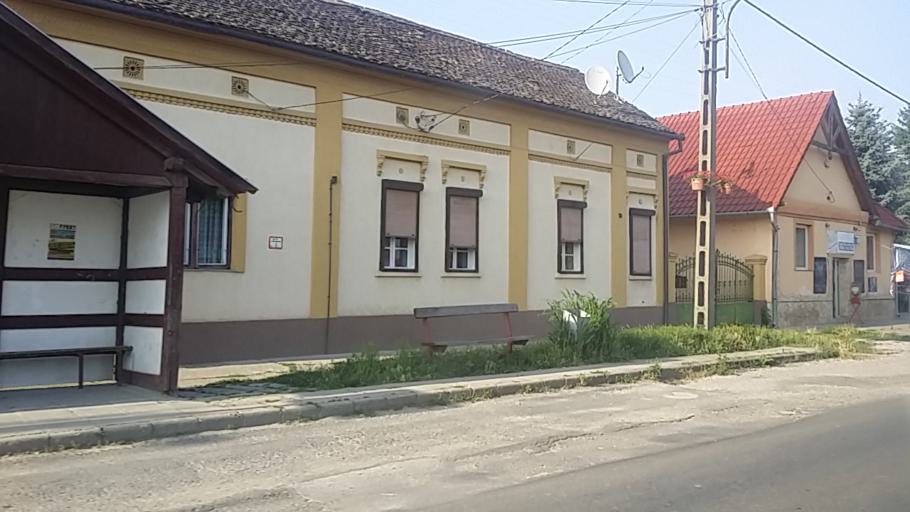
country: HU
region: Baranya
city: Villany
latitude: 45.8479
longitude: 18.3950
